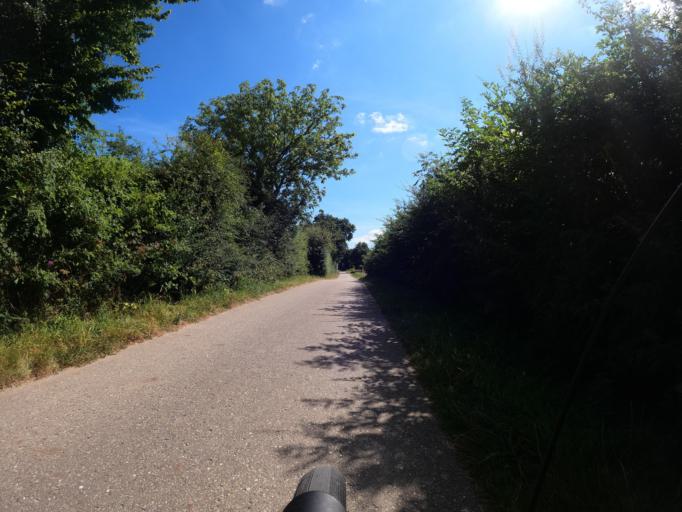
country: DE
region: Schleswig-Holstein
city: Dollerup
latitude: 54.7783
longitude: 9.6846
